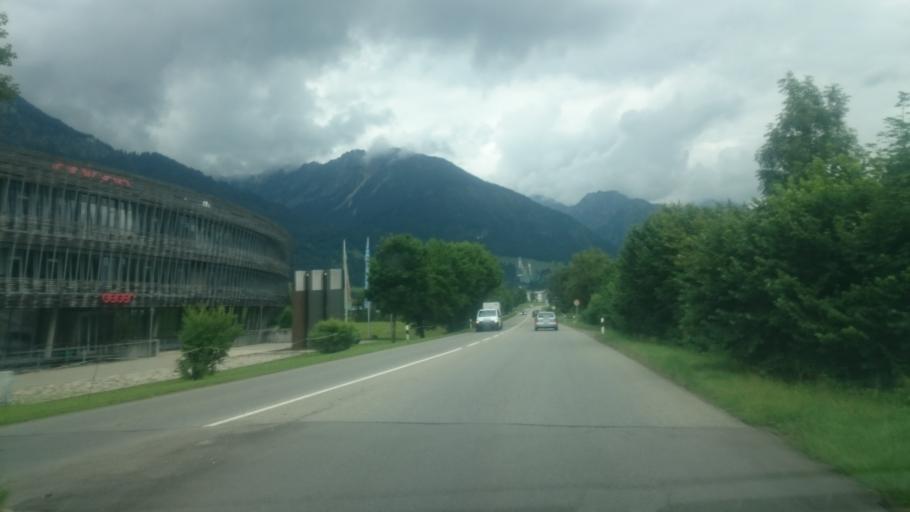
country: DE
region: Bavaria
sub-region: Swabia
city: Oberstdorf
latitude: 47.4241
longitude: 10.2681
